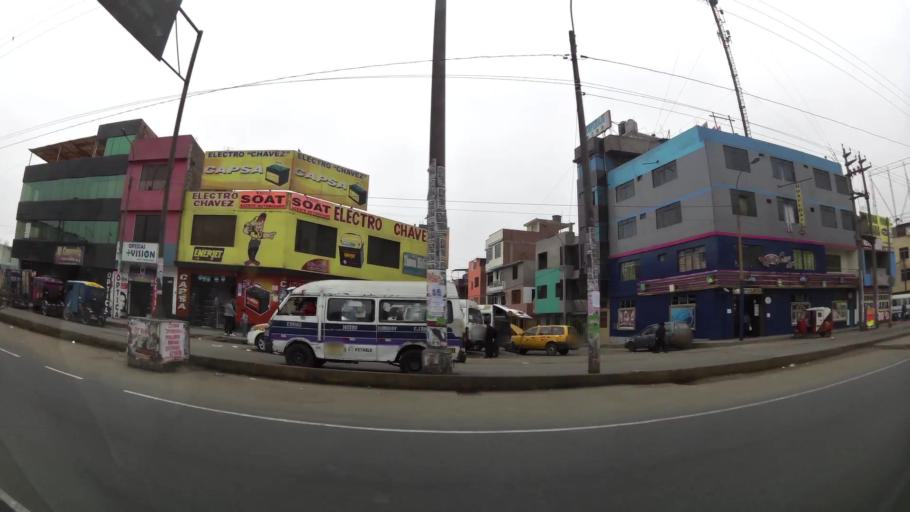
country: PE
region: Lima
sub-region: Lima
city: Independencia
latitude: -11.9331
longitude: -77.0465
